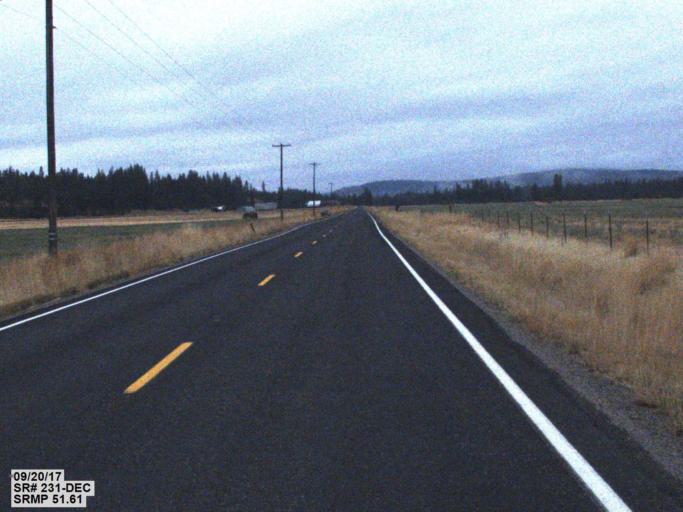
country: US
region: Washington
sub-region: Spokane County
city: Deer Park
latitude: 47.9204
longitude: -117.7880
